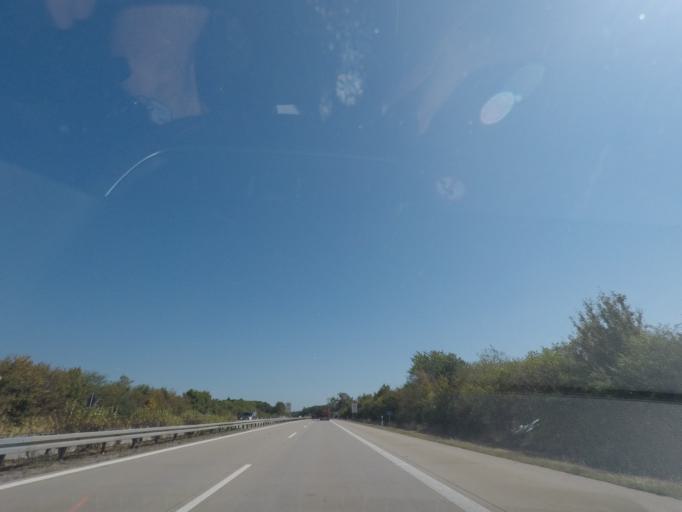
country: DE
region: Brandenburg
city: Grosskmehlen
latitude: 51.3630
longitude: 13.7384
